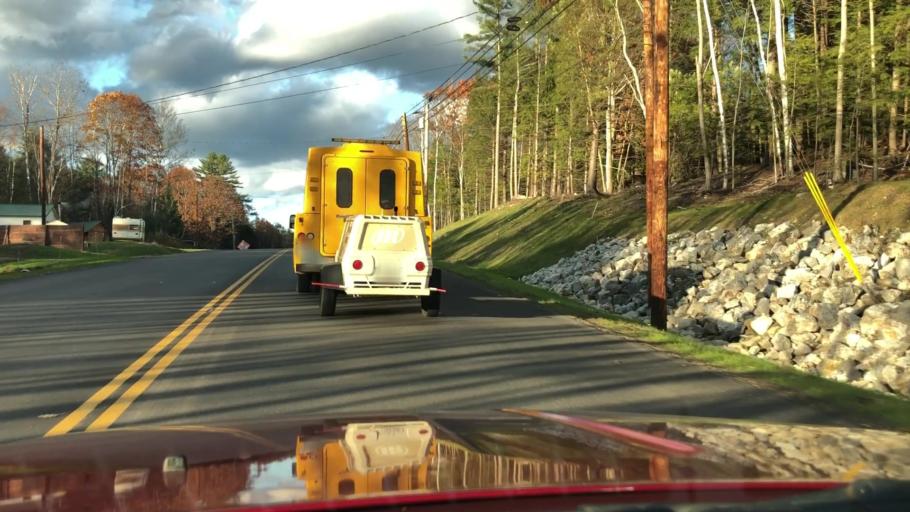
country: US
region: Maine
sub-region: Oxford County
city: Peru
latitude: 44.5214
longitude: -70.4081
